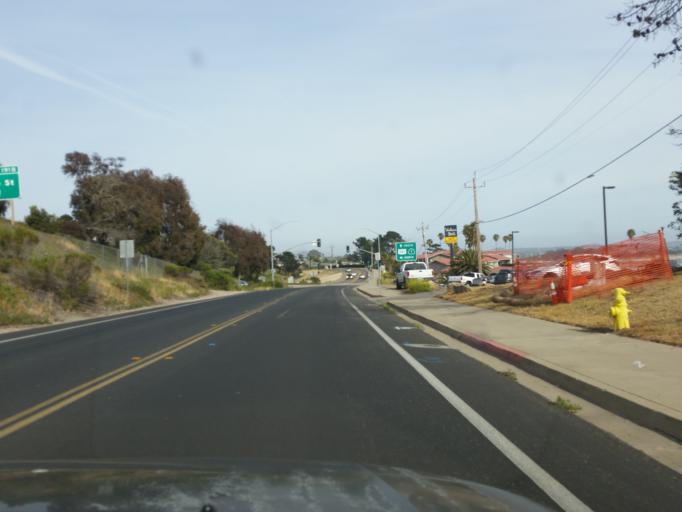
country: US
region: California
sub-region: San Luis Obispo County
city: Pismo Beach
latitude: 35.1510
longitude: -120.6560
